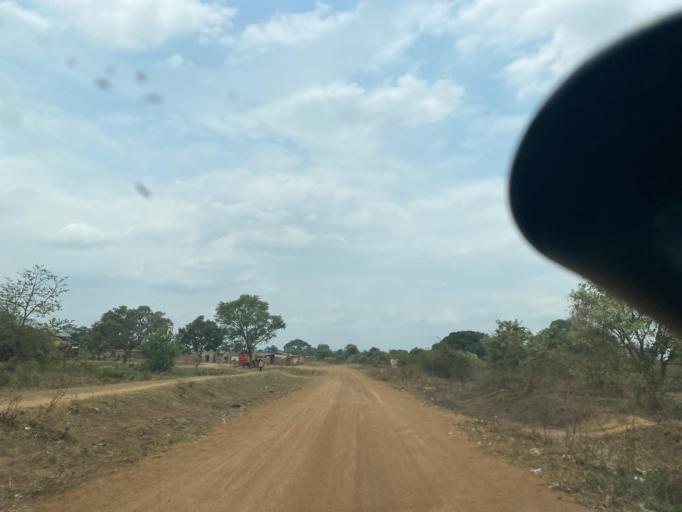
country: ZM
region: Lusaka
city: Chongwe
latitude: -15.5064
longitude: 28.8165
